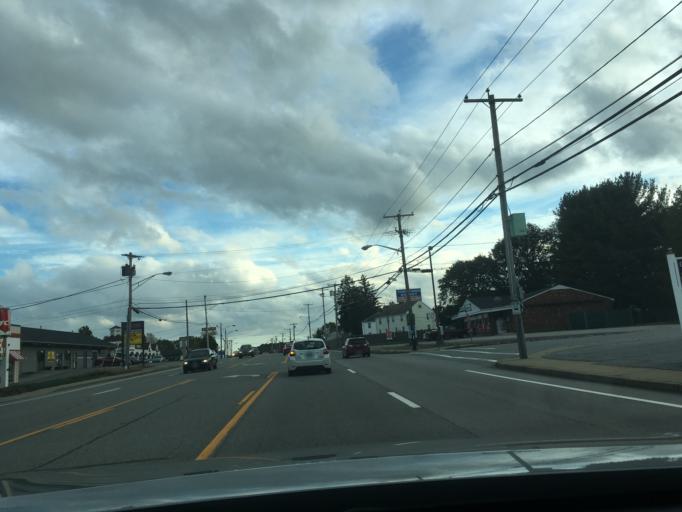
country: US
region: Rhode Island
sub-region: Kent County
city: East Greenwich
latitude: 41.6142
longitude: -71.4577
